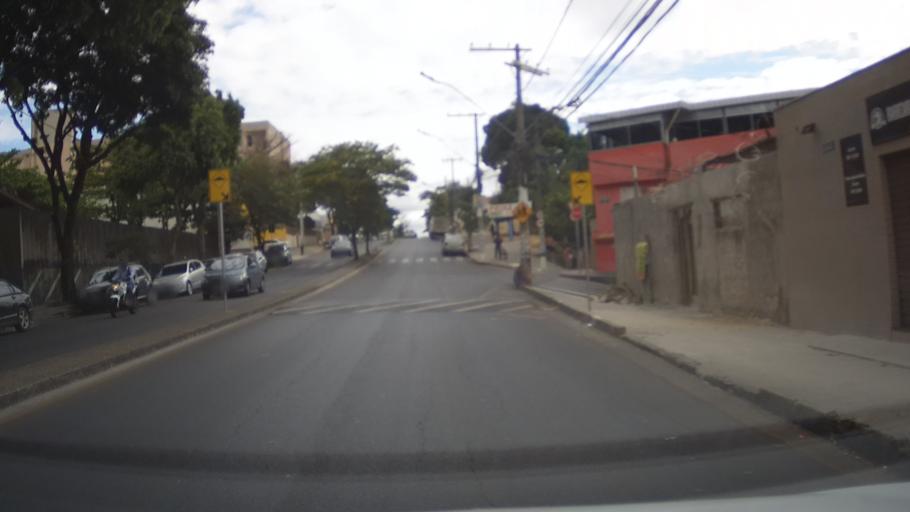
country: BR
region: Minas Gerais
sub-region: Belo Horizonte
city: Belo Horizonte
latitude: -19.8426
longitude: -43.9526
